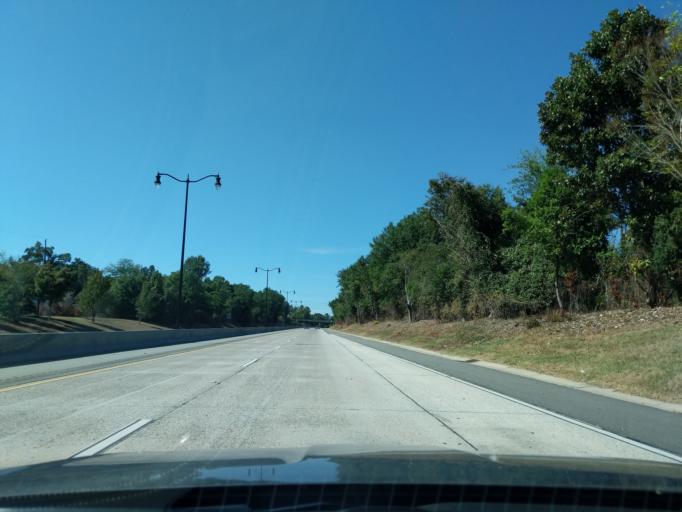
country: US
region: Georgia
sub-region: Richmond County
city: Augusta
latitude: 33.4857
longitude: -82.0019
